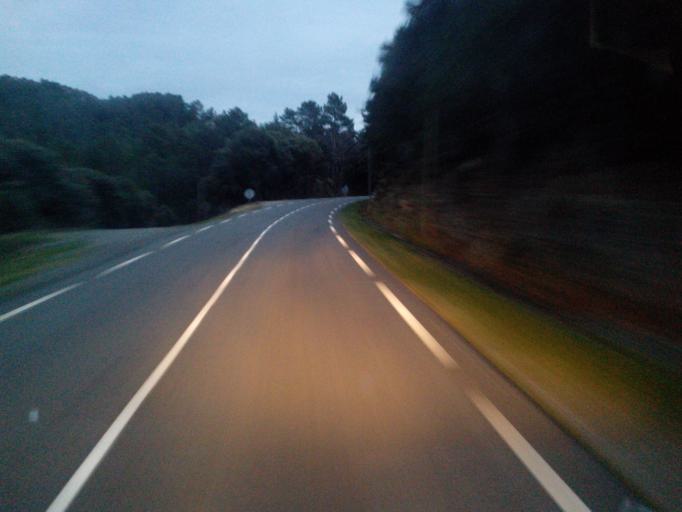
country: FR
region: Languedoc-Roussillon
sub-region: Departement du Gard
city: Saint-Jean-du-Gard
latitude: 44.1358
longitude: 3.8367
